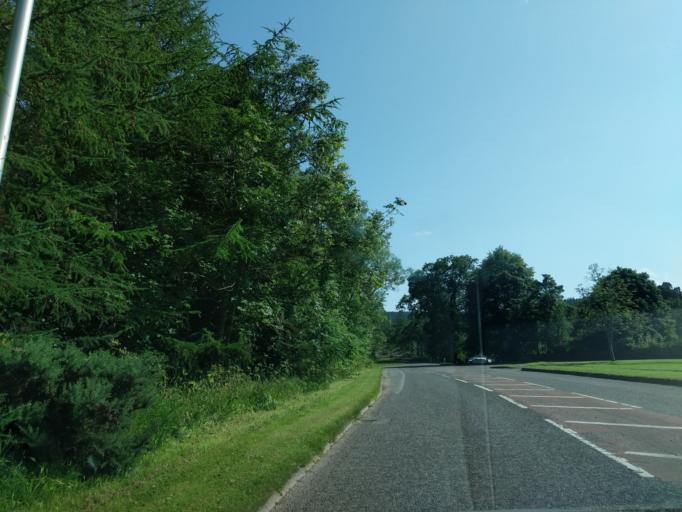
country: GB
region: Scotland
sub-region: Moray
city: Fochabers
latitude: 57.6097
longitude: -3.0888
